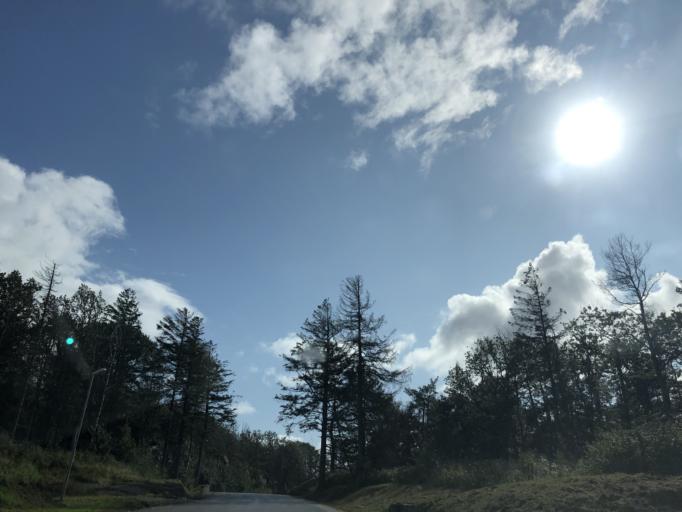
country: SE
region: Vaestra Goetaland
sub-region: Goteborg
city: Majorna
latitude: 57.7142
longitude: 11.8507
